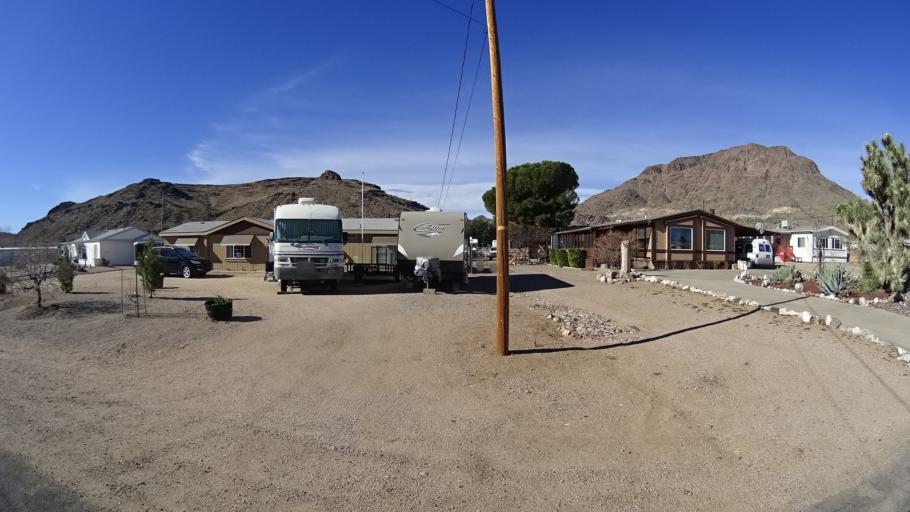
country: US
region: Arizona
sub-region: Mohave County
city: New Kingman-Butler
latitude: 35.2687
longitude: -114.0468
